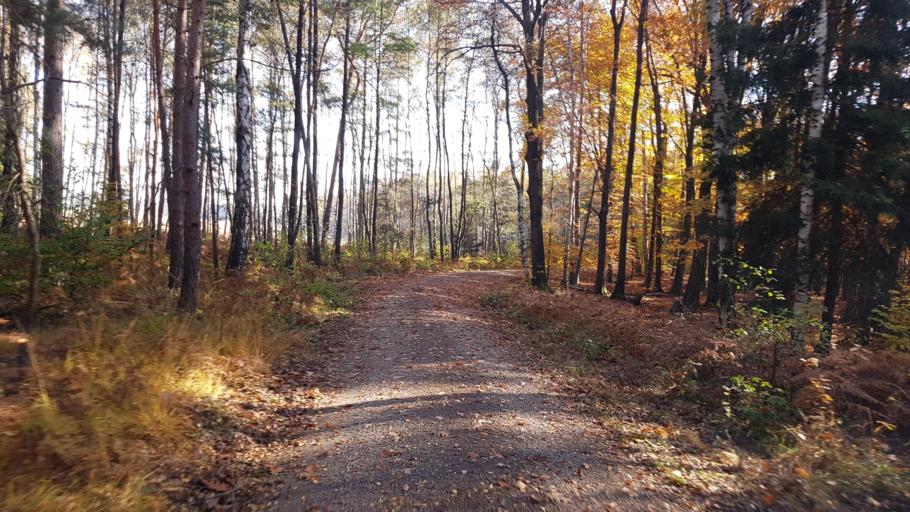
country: DE
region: Brandenburg
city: Ruckersdorf
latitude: 51.5667
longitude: 13.6187
